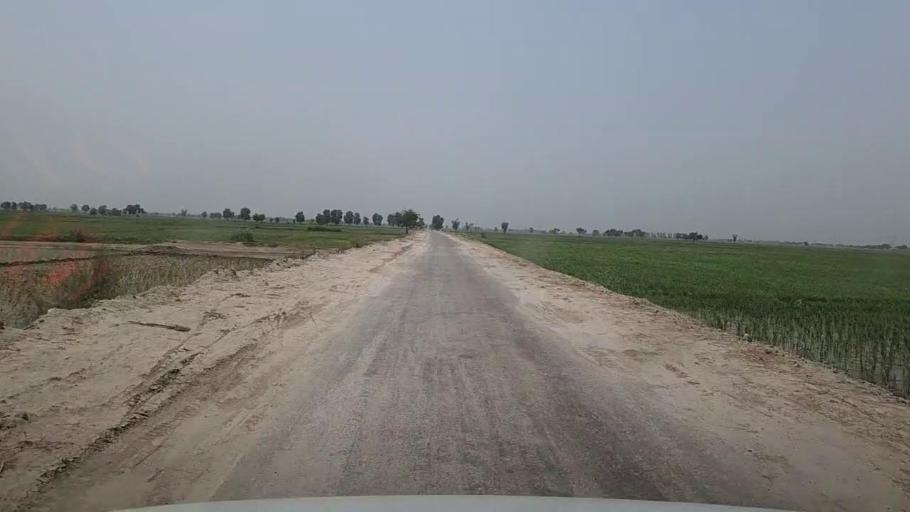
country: PK
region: Sindh
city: Sita Road
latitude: 27.0880
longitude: 67.9131
